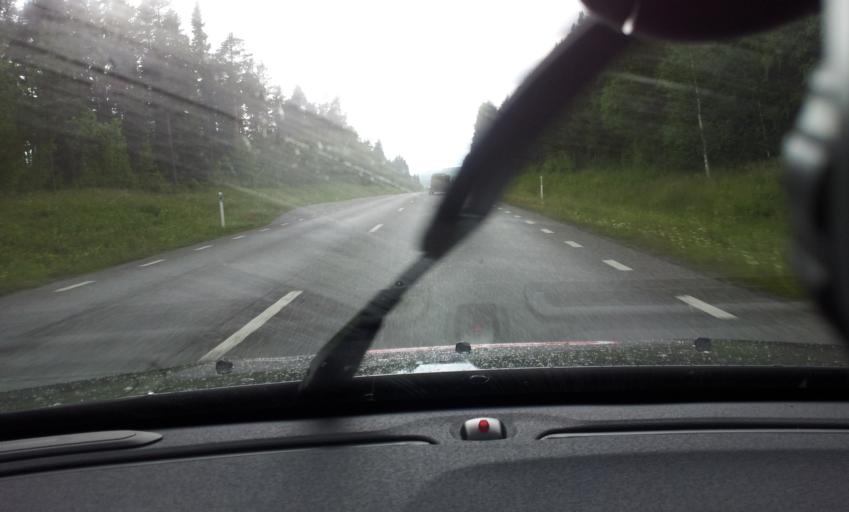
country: SE
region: Jaemtland
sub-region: Krokoms Kommun
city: Valla
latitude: 63.3098
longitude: 13.7980
